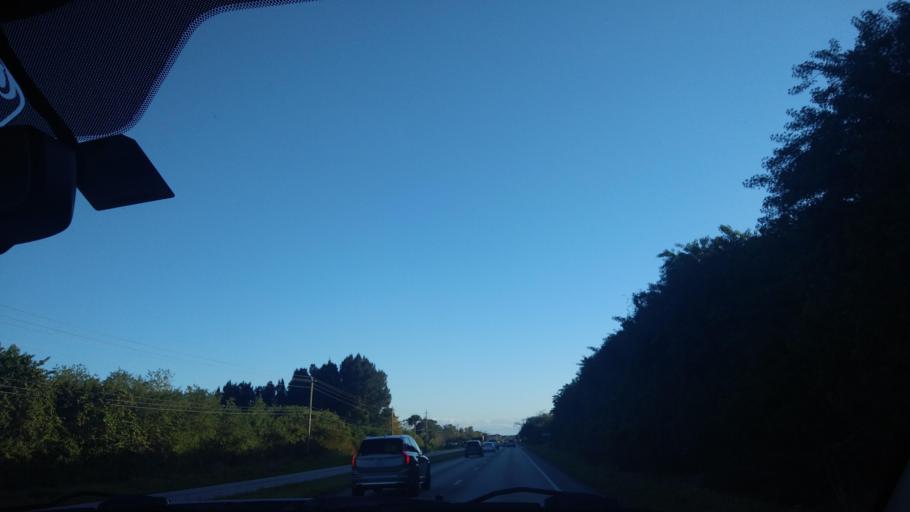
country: US
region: Florida
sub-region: Indian River County
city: Winter Beach
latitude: 27.7245
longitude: -80.4229
